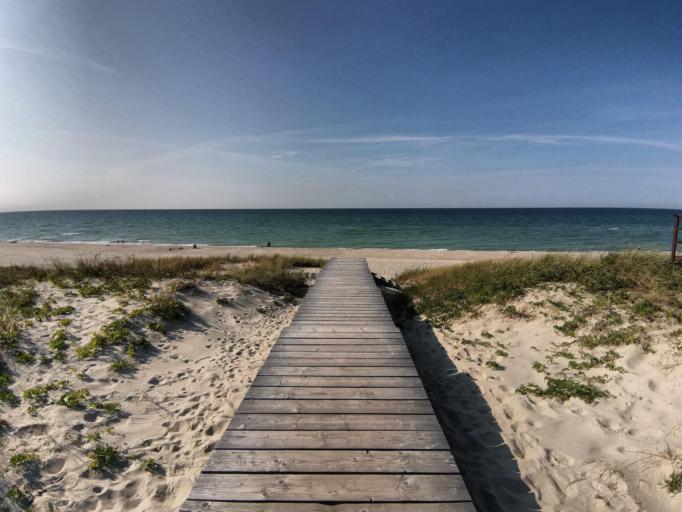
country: LT
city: Nida
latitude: 55.1646
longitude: 20.8167
